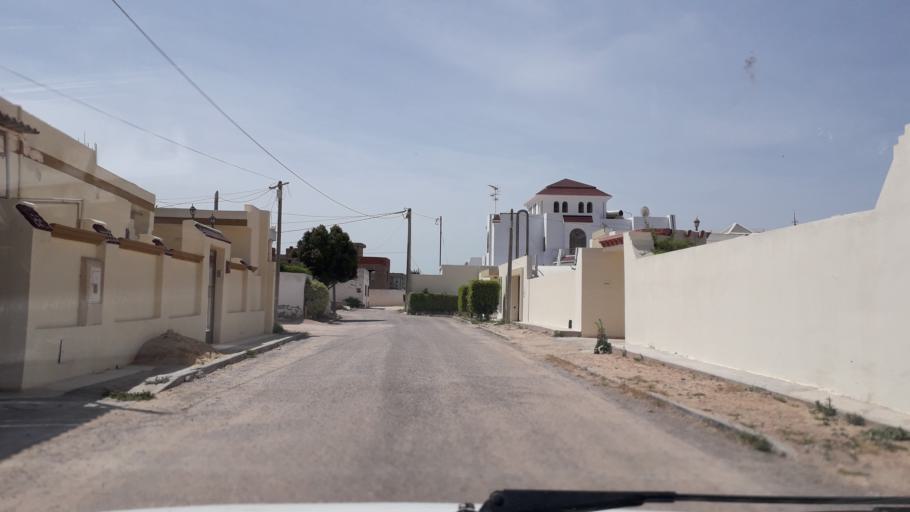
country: TN
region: Safaqis
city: Al Qarmadah
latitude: 34.7998
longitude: 10.7627
